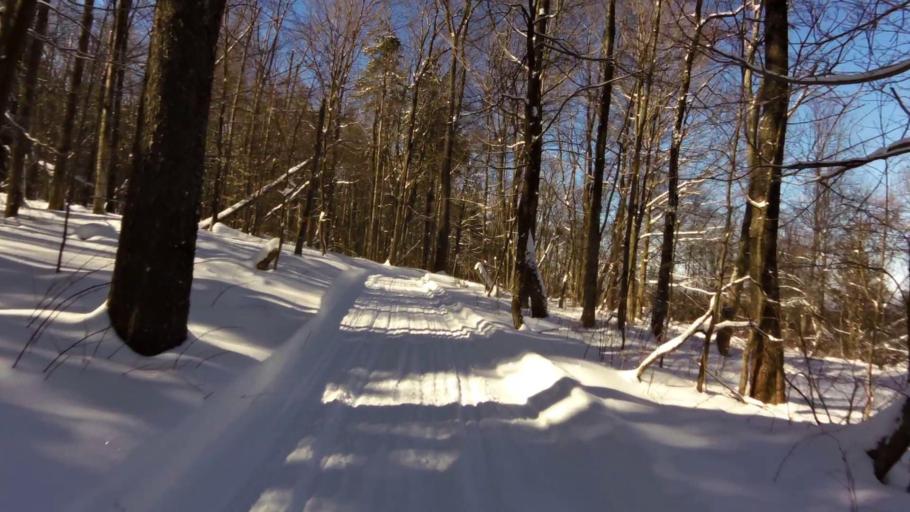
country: US
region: New York
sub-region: Chautauqua County
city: Fredonia
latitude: 42.3484
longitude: -79.1959
